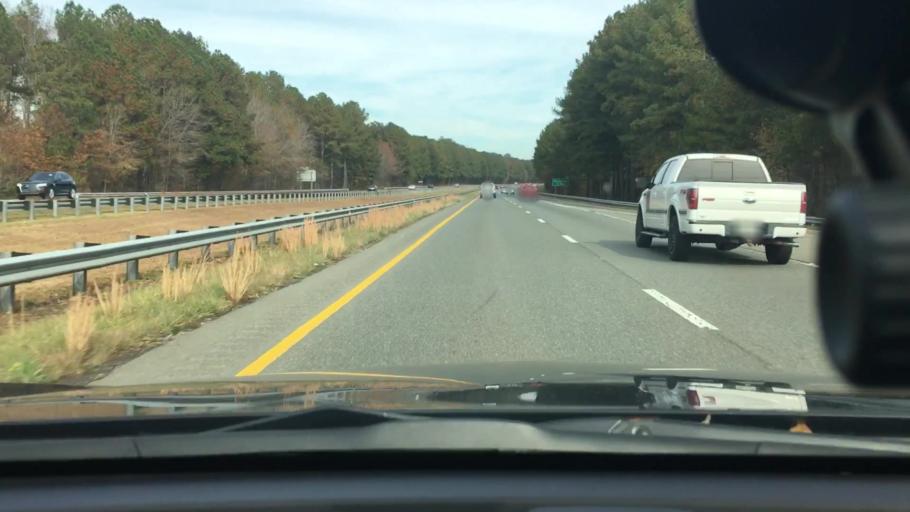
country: US
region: North Carolina
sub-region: Chatham County
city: Farmville
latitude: 35.5634
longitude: -79.1513
